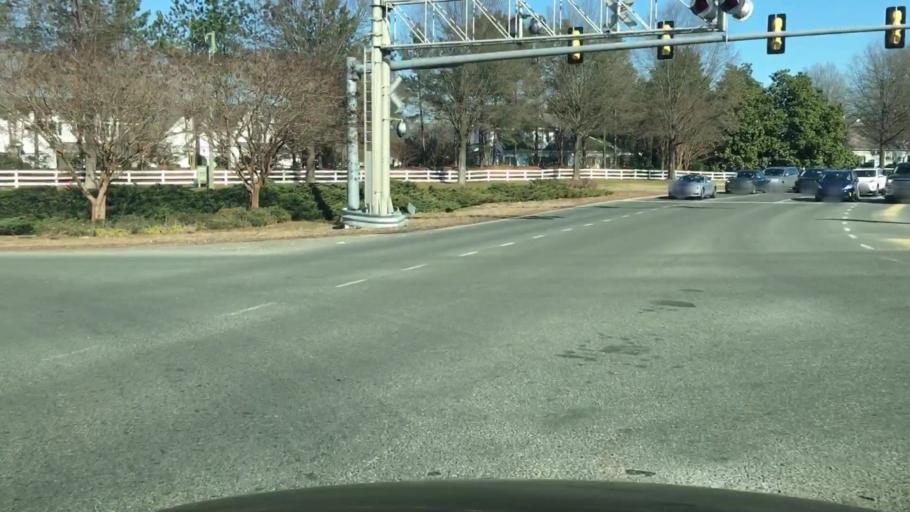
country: US
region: Virginia
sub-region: Chesterfield County
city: Bon Air
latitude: 37.5222
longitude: -77.6119
